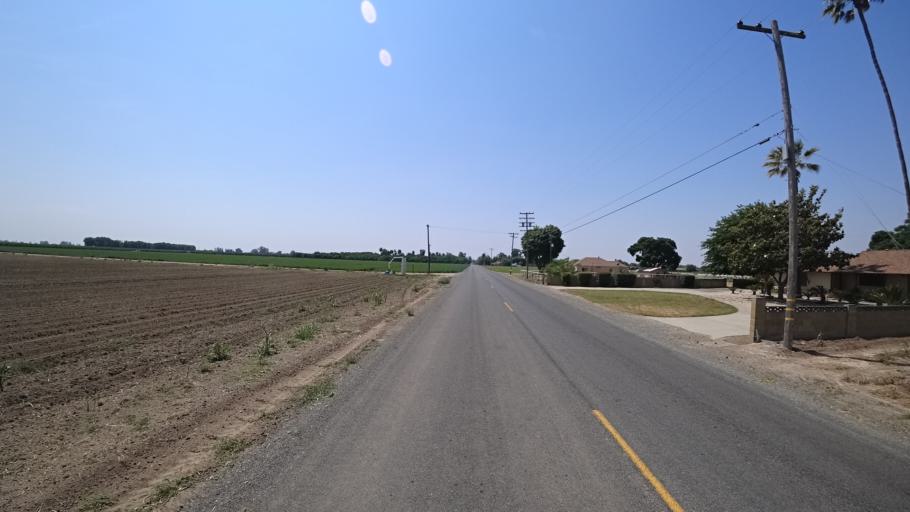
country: US
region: California
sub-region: Kings County
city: Lemoore
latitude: 36.3248
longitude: -119.7628
